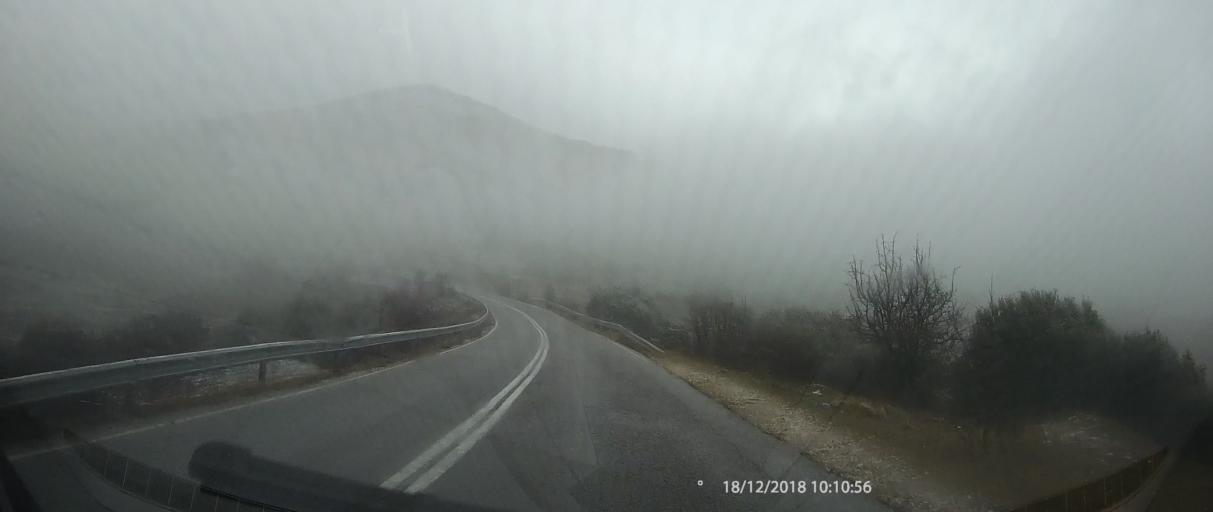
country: GR
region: Thessaly
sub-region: Nomos Larisis
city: Livadi
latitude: 40.0906
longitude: 22.2103
